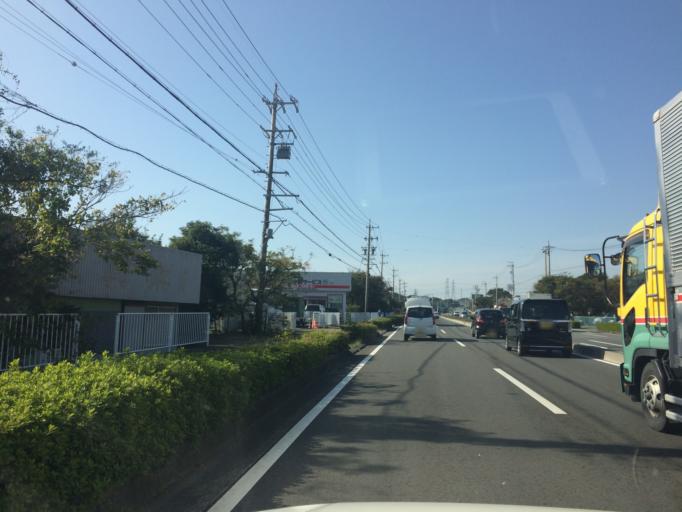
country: JP
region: Shizuoka
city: Oyama
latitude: 34.6235
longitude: 138.1640
